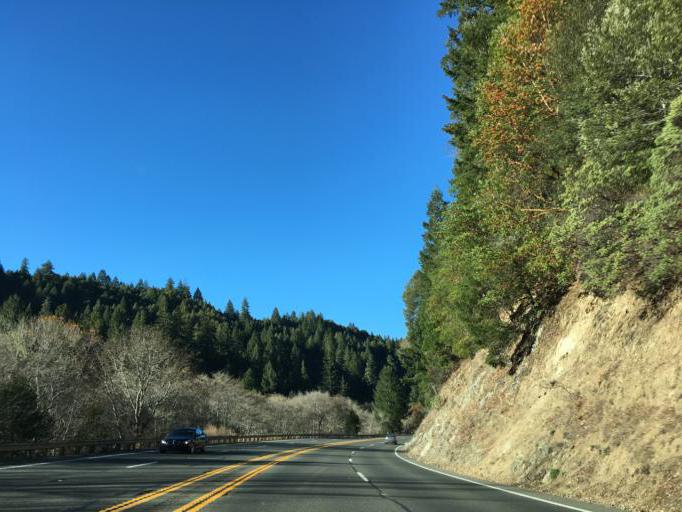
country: US
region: California
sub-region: Mendocino County
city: Brooktrails
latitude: 39.5282
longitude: -123.4025
